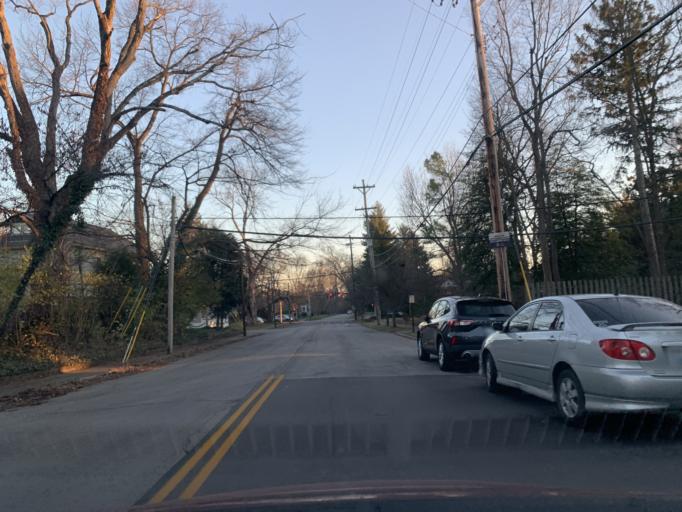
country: US
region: Kentucky
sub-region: Jefferson County
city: Saint Matthews
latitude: 38.2495
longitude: -85.6814
